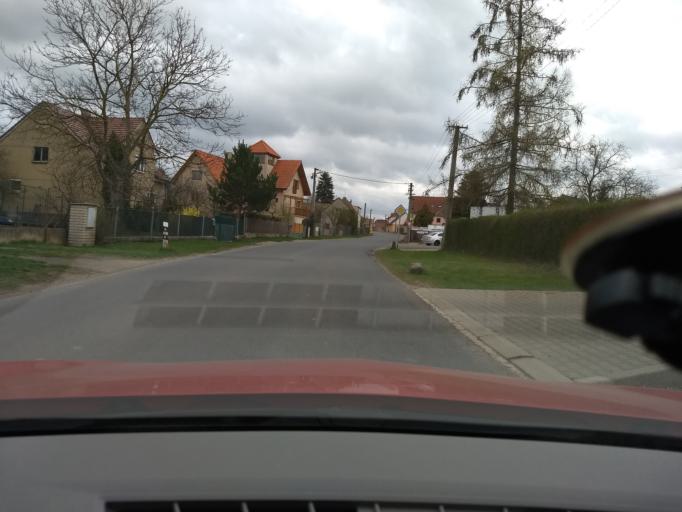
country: CZ
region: Central Bohemia
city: Unhost'
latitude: 50.0714
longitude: 14.1597
